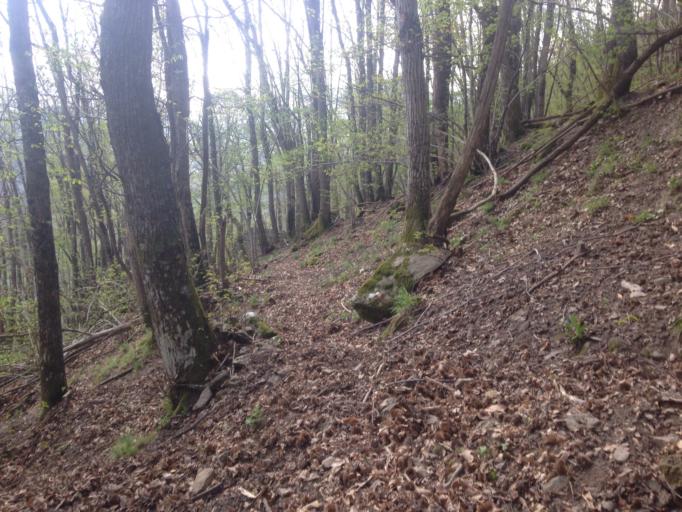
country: IT
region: Emilia-Romagna
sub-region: Provincia di Bologna
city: Lizzano in Belvedere
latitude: 44.1545
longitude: 10.8895
